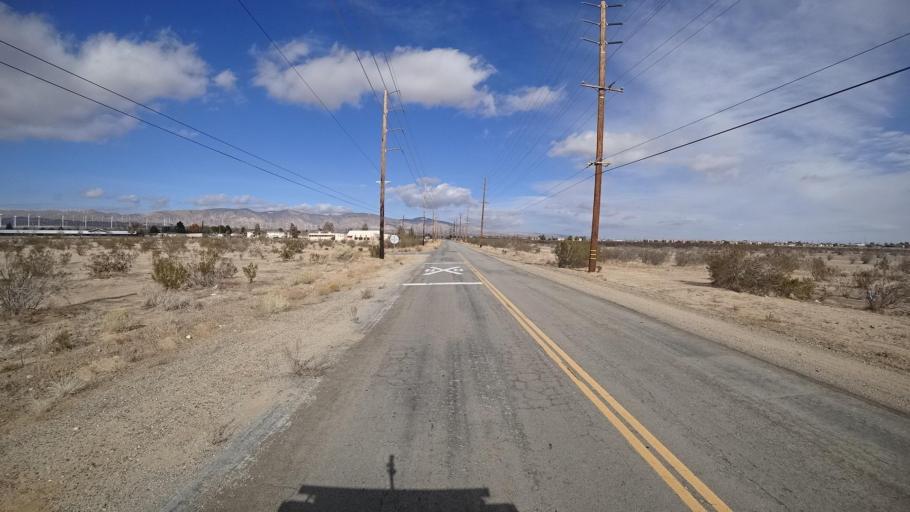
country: US
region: California
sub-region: Kern County
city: Mojave
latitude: 35.0475
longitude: -118.1855
